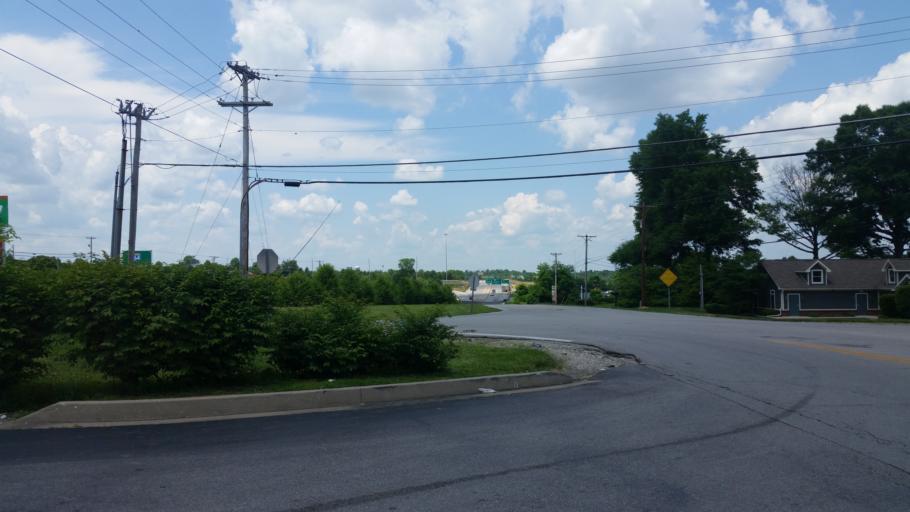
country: US
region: Kentucky
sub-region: Franklin County
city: Frankfort
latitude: 38.1507
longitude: -84.8948
